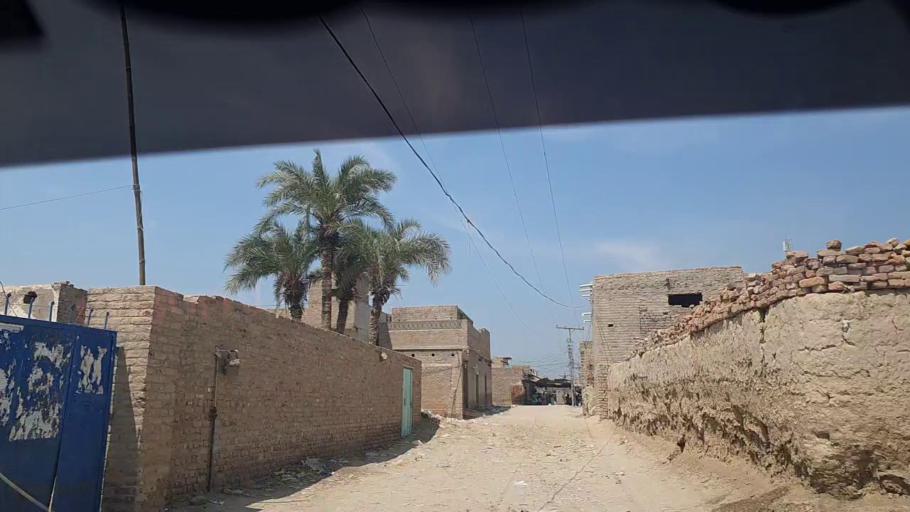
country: PK
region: Sindh
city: Thul
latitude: 28.1789
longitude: 68.7262
